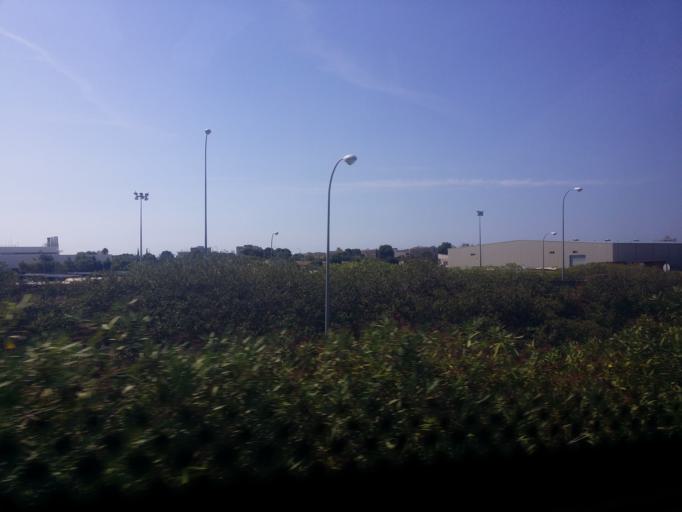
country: ES
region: Balearic Islands
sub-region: Illes Balears
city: s'Arenal
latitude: 39.5445
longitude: 2.7205
